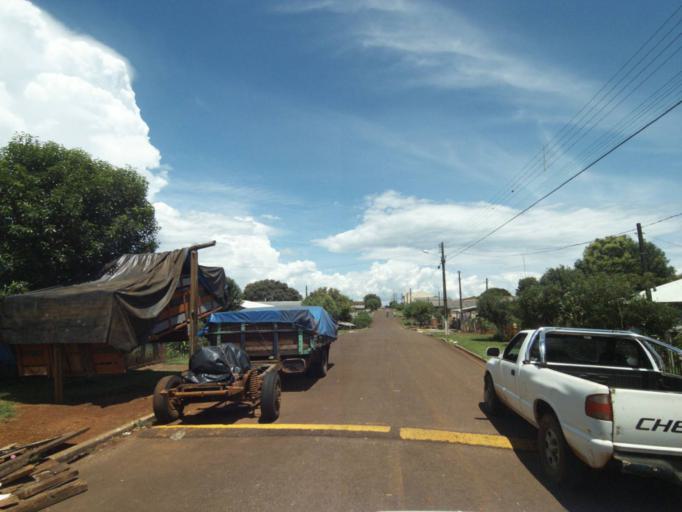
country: BR
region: Parana
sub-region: Guaraniacu
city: Guaraniacu
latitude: -25.0893
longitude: -52.8764
